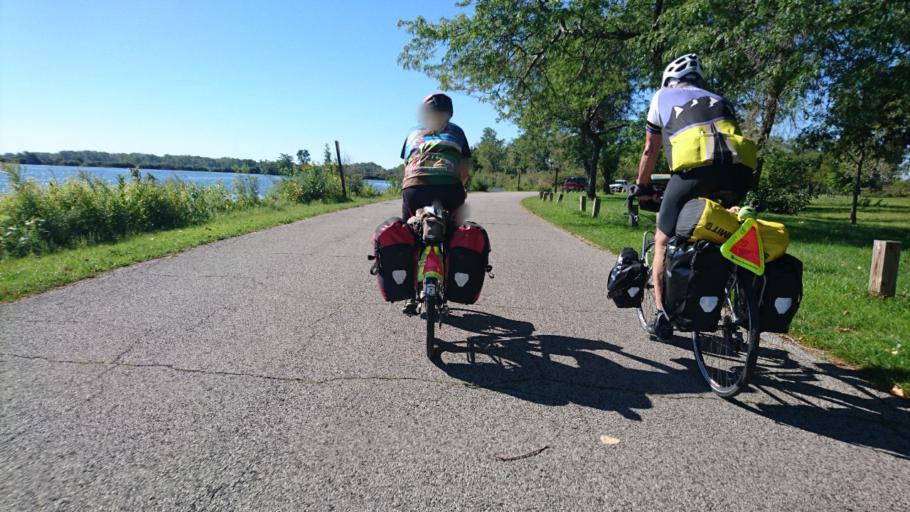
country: US
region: Illinois
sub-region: Cook County
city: Burnham
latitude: 41.6677
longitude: -87.5368
